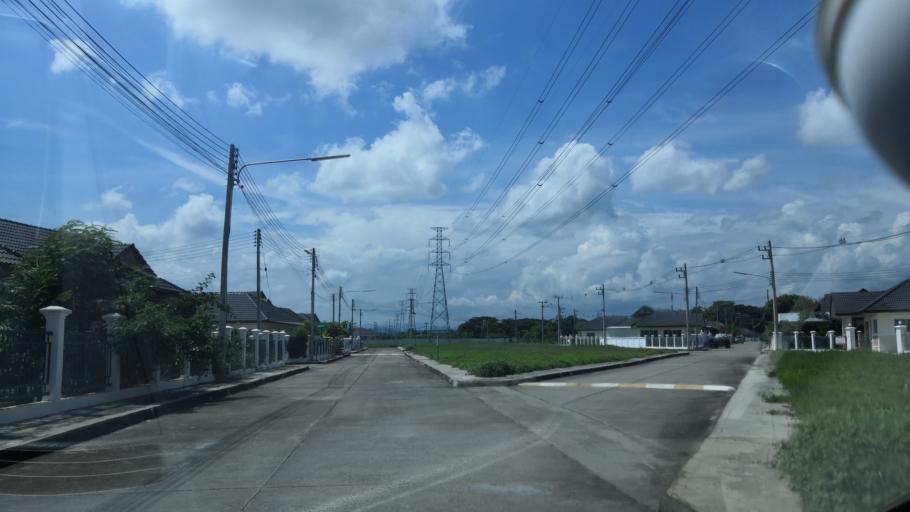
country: TH
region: Chiang Mai
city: Hang Dong
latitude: 18.7182
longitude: 98.9599
